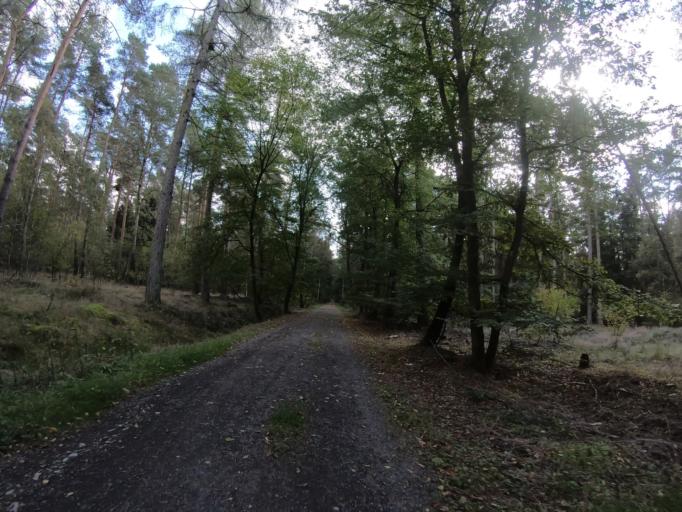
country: DE
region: Lower Saxony
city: Isenbuttel
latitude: 52.4515
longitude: 10.5730
